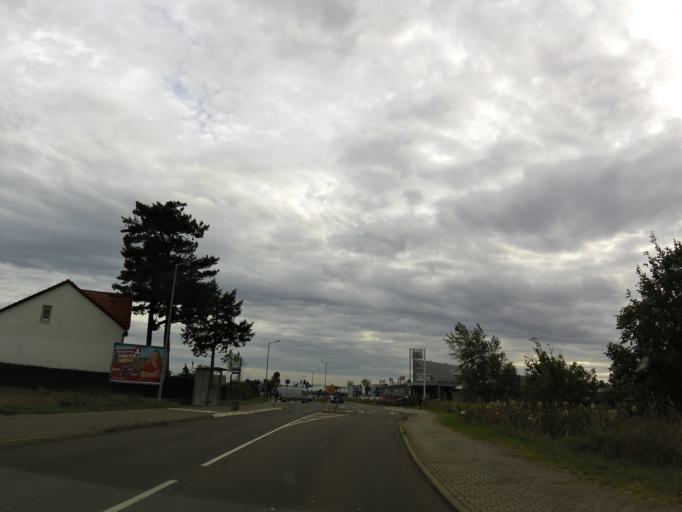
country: DE
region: Saxony
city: Schkeuditz
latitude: 51.3487
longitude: 12.2630
